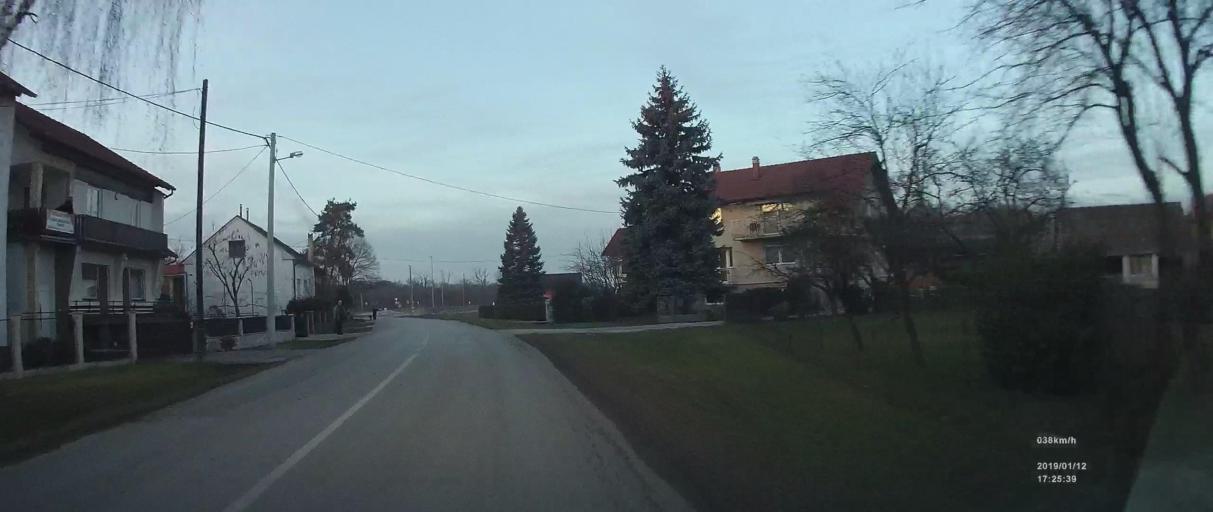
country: HR
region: Zagrebacka
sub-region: Grad Velika Gorica
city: Velika Gorica
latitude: 45.7328
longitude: 16.1014
